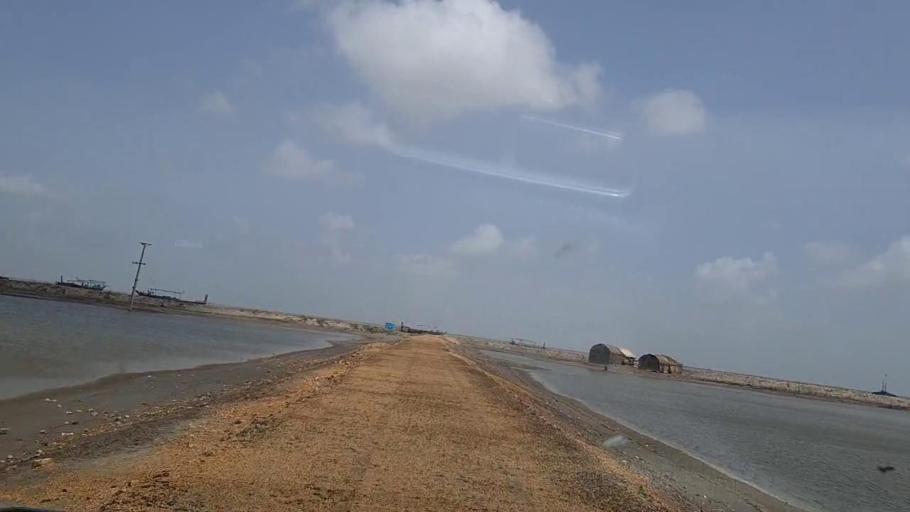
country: PK
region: Sindh
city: Keti Bandar
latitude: 24.1276
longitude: 67.4682
